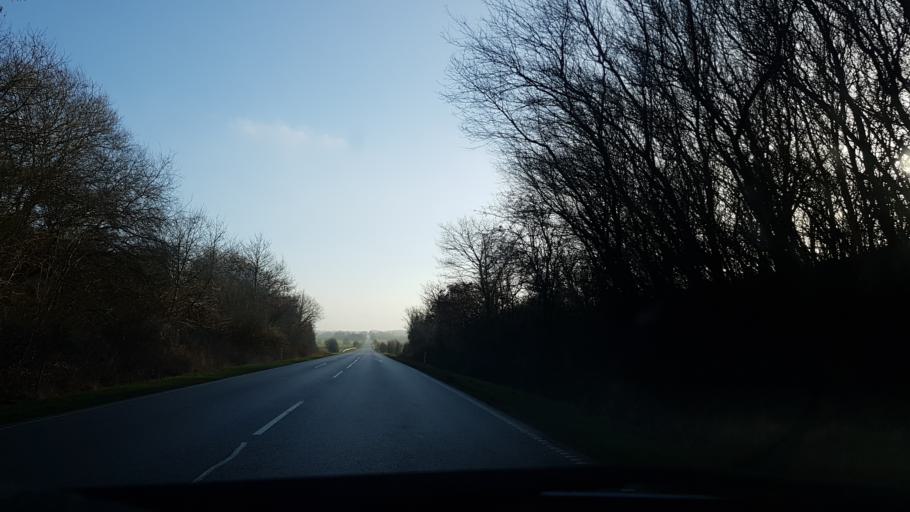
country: DK
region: South Denmark
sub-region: Tonder Kommune
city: Toftlund
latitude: 55.2496
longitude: 9.1501
